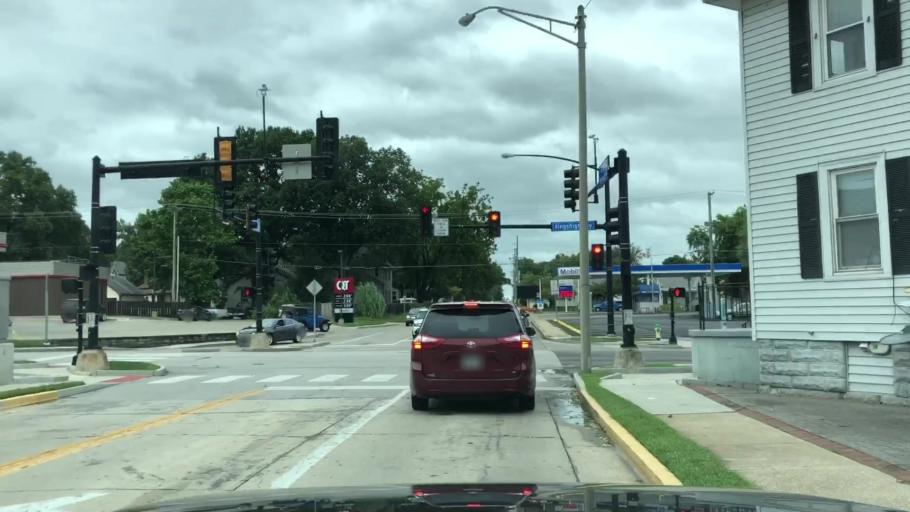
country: US
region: Missouri
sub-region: Saint Charles County
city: Saint Charles
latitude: 38.7870
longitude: -90.4929
